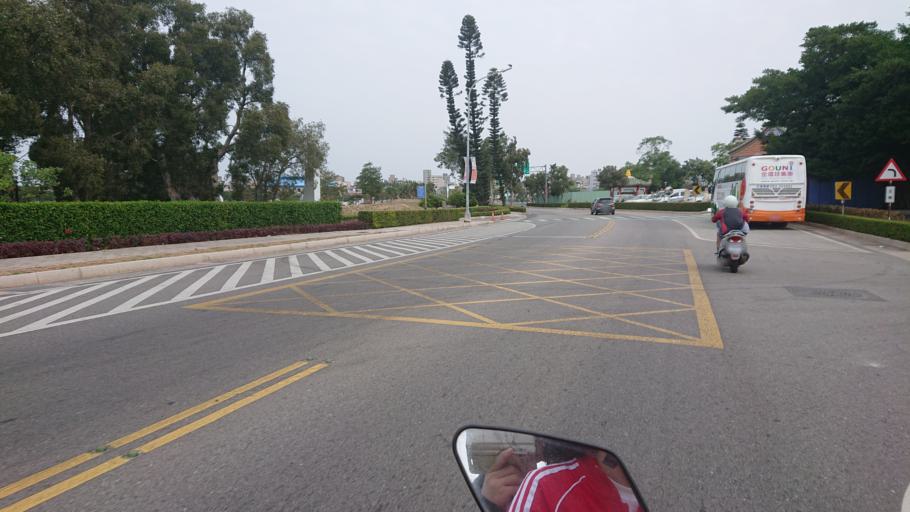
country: TW
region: Fukien
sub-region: Kinmen
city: Jincheng
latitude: 24.4252
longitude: 118.3155
